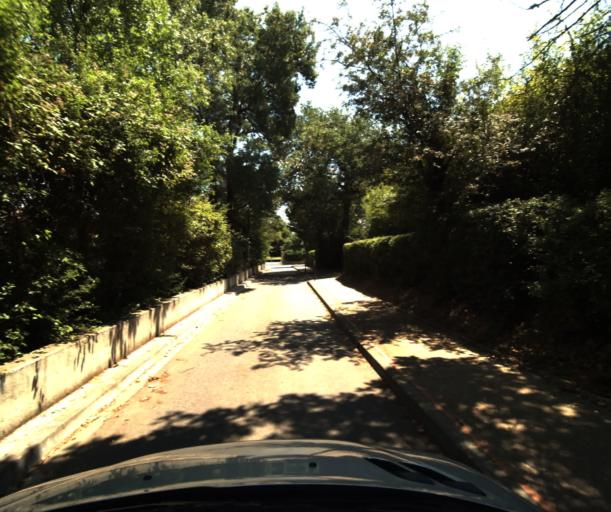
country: FR
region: Midi-Pyrenees
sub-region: Departement de la Haute-Garonne
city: Saint-Lys
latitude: 43.5112
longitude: 1.1765
